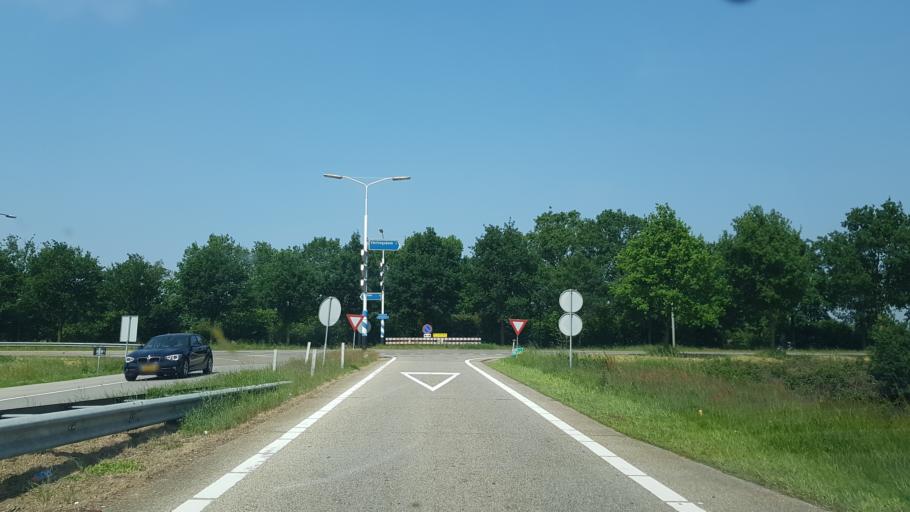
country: NL
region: North Brabant
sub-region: Gemeente Boxmeer
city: Overloon
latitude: 51.5854
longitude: 5.9815
